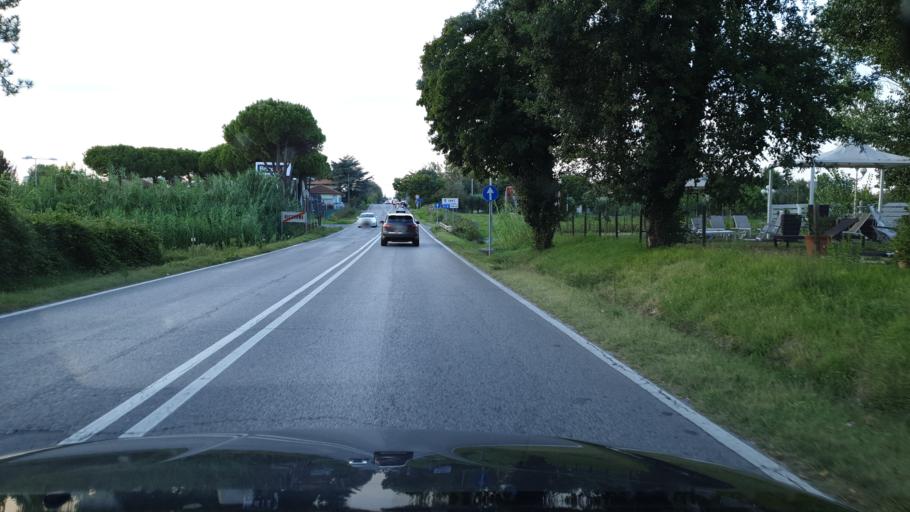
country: IT
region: Emilia-Romagna
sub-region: Provincia di Rimini
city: Rivazzurra
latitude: 44.0197
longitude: 12.6259
